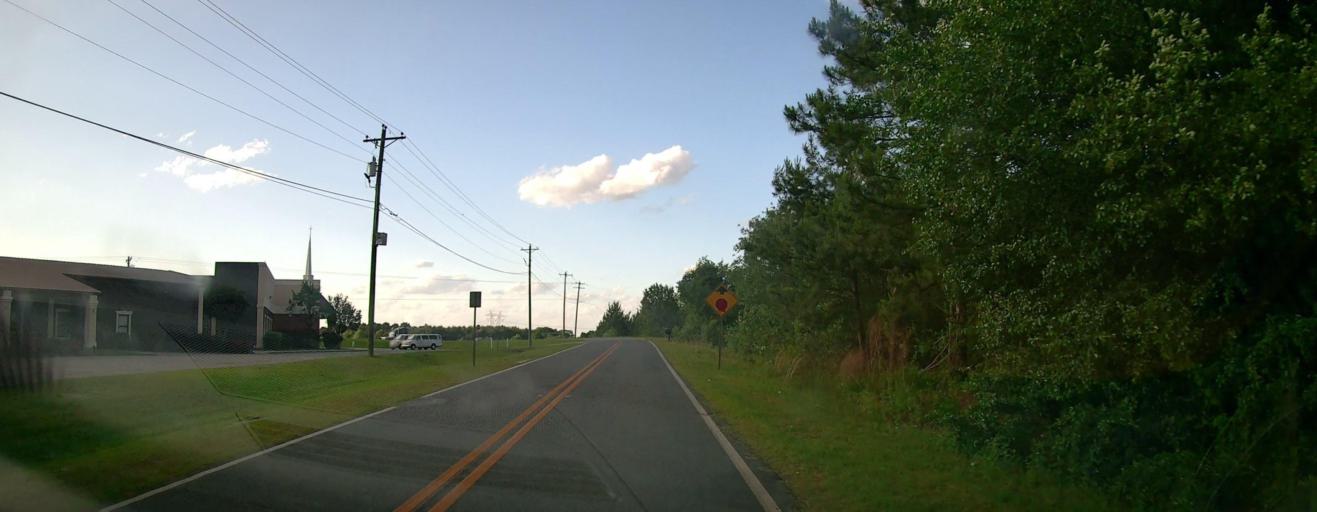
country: US
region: Georgia
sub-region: Peach County
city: Byron
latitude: 32.6366
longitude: -83.7671
